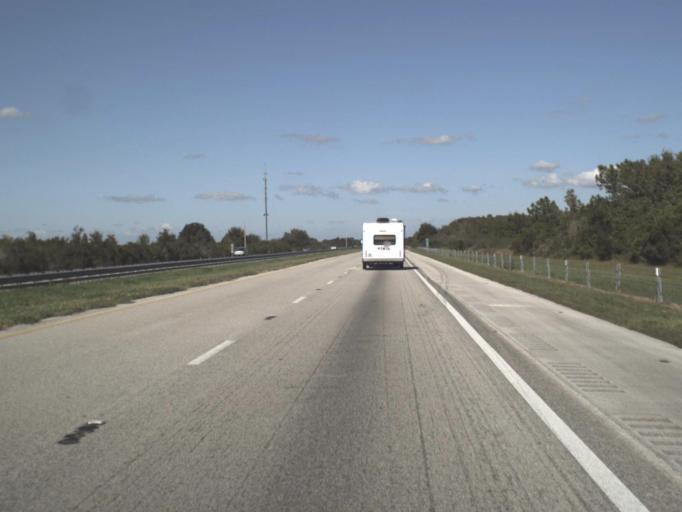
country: US
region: Florida
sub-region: Osceola County
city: Saint Cloud
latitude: 28.0197
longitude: -81.1789
